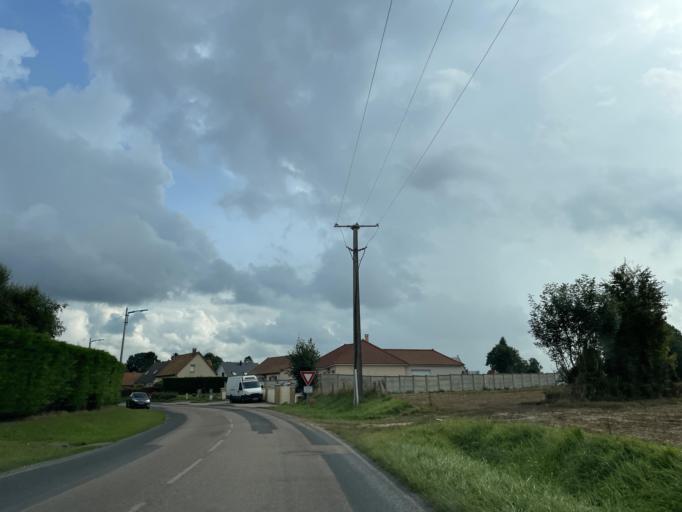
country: FR
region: Haute-Normandie
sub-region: Departement de la Seine-Maritime
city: Envermeu
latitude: 49.9332
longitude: 1.2754
